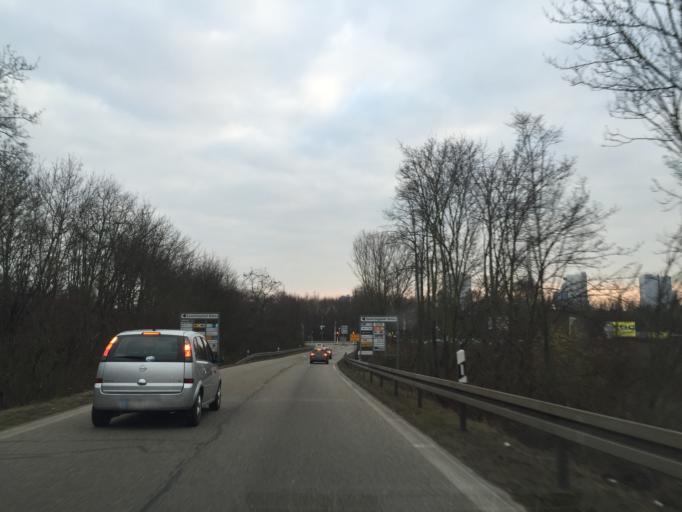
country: DE
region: Rheinland-Pfalz
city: Altrip
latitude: 49.4559
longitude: 8.5104
